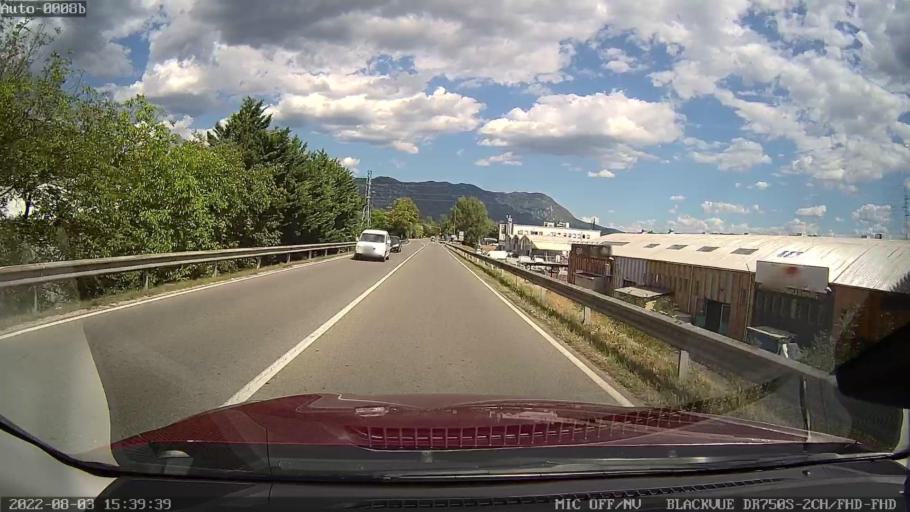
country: SI
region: Nova Gorica
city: Kromberk
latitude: 45.9573
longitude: 13.6594
